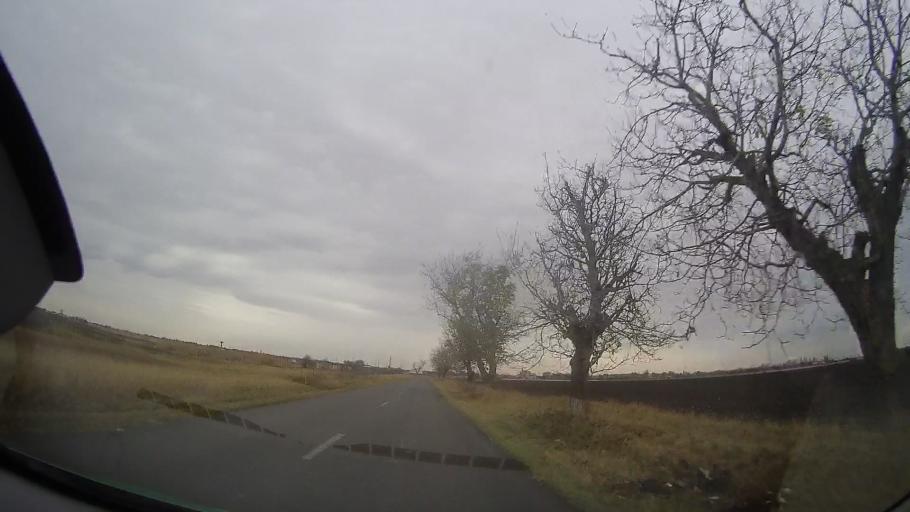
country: RO
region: Prahova
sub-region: Oras Mizil
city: Mizil
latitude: 45.0083
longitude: 26.4206
